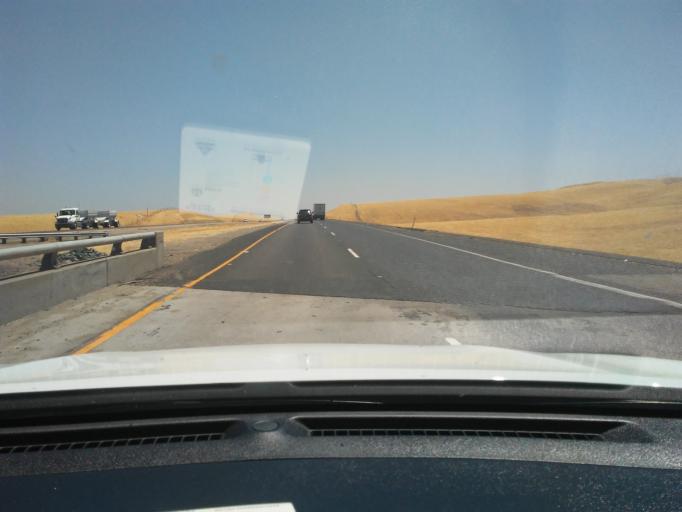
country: US
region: California
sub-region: San Joaquin County
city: Tracy
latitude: 37.7018
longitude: -121.5063
